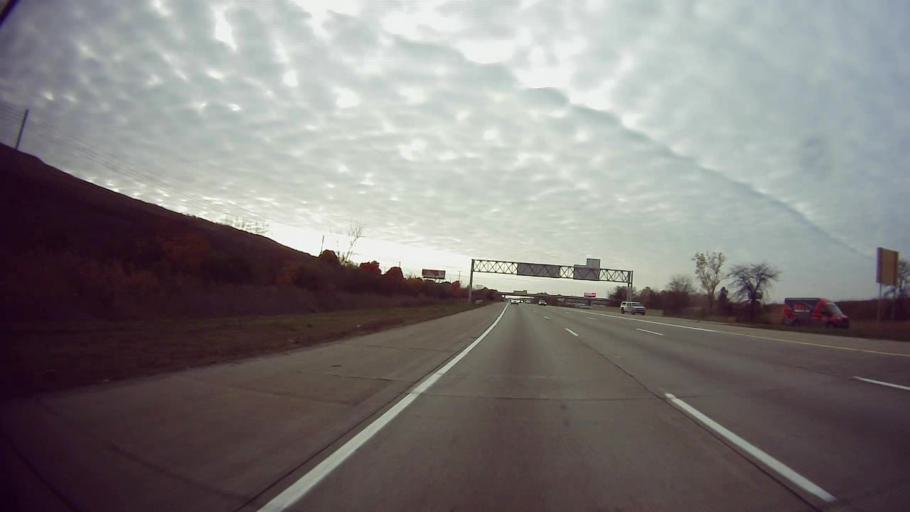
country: US
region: Michigan
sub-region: Wayne County
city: Woodhaven
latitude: 42.1866
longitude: -83.2432
